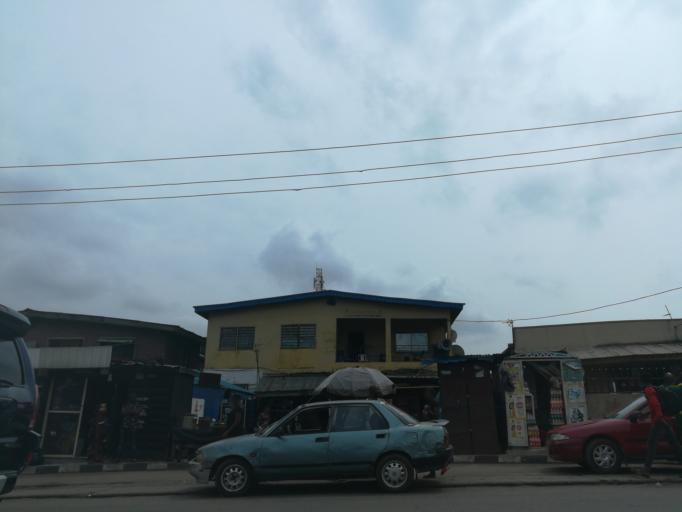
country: NG
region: Lagos
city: Ikeja
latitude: 6.6018
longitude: 3.3634
